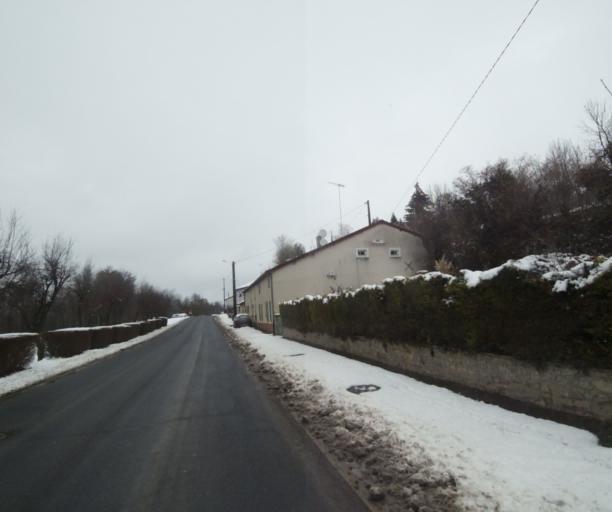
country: FR
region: Champagne-Ardenne
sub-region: Departement de la Haute-Marne
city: Wassy
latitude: 48.4733
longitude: 4.9713
